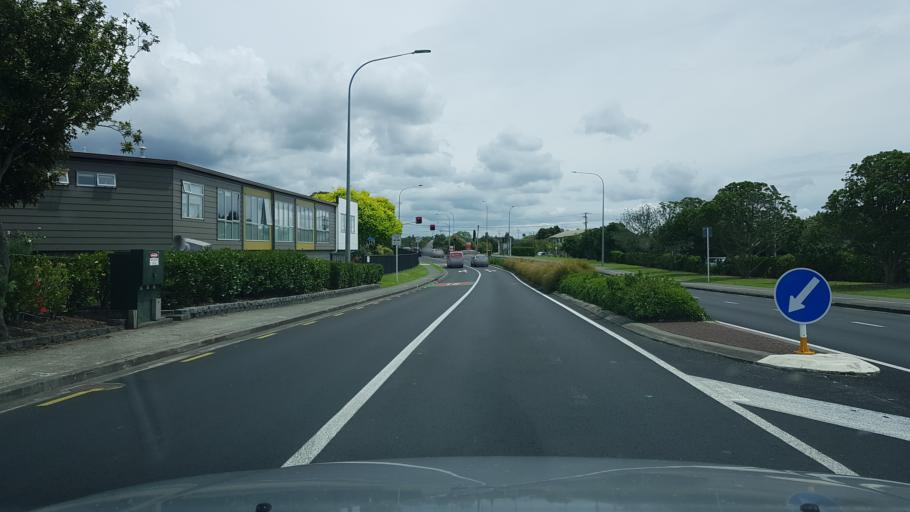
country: NZ
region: Auckland
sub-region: Auckland
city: North Shore
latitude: -36.7973
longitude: 174.7553
